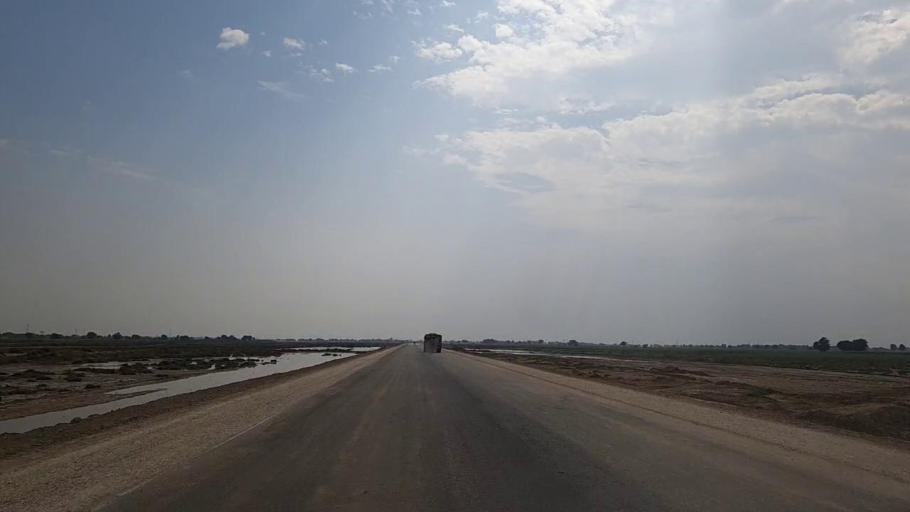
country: PK
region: Sindh
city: Naukot
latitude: 24.9966
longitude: 69.2854
